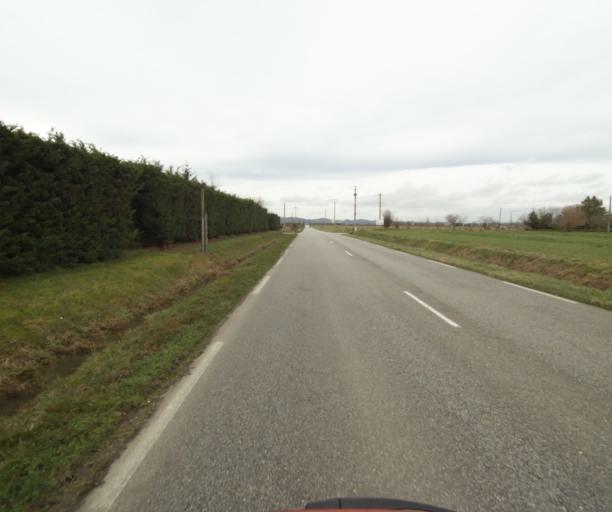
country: FR
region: Midi-Pyrenees
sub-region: Departement de l'Ariege
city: La Tour-du-Crieu
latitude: 43.0937
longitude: 1.6733
